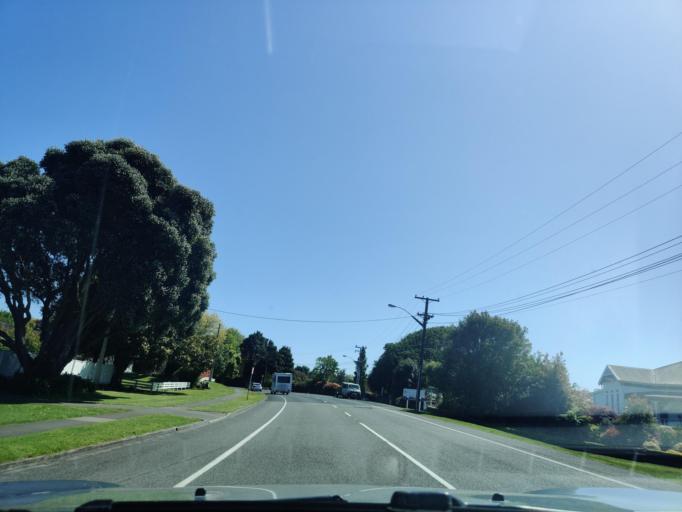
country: NZ
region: Manawatu-Wanganui
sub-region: Wanganui District
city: Wanganui
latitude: -39.9114
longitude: 175.0264
